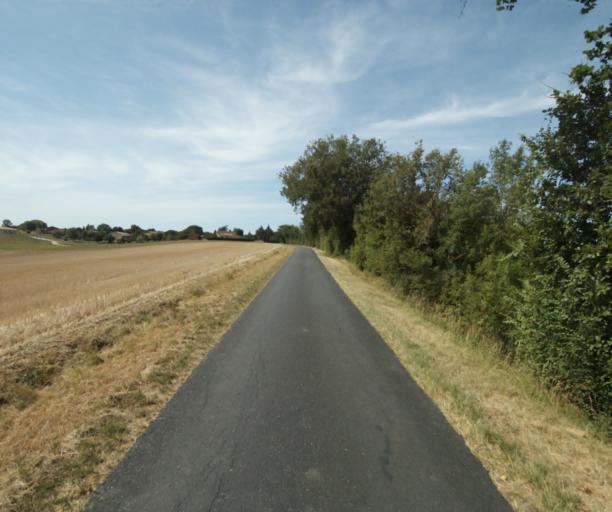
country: FR
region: Midi-Pyrenees
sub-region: Departement du Tarn
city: Puylaurens
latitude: 43.5307
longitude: 2.0206
